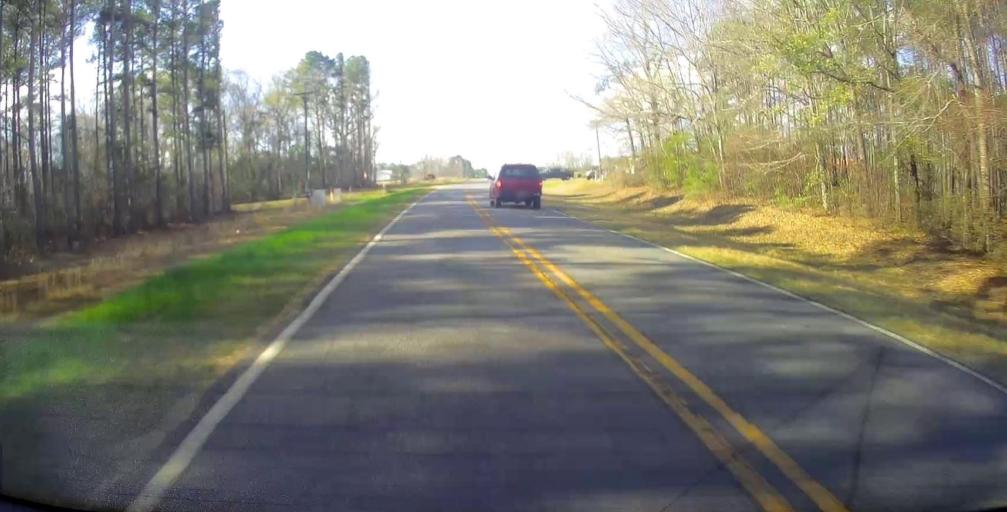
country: US
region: Georgia
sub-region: Laurens County
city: Dublin
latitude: 32.5960
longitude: -83.0701
